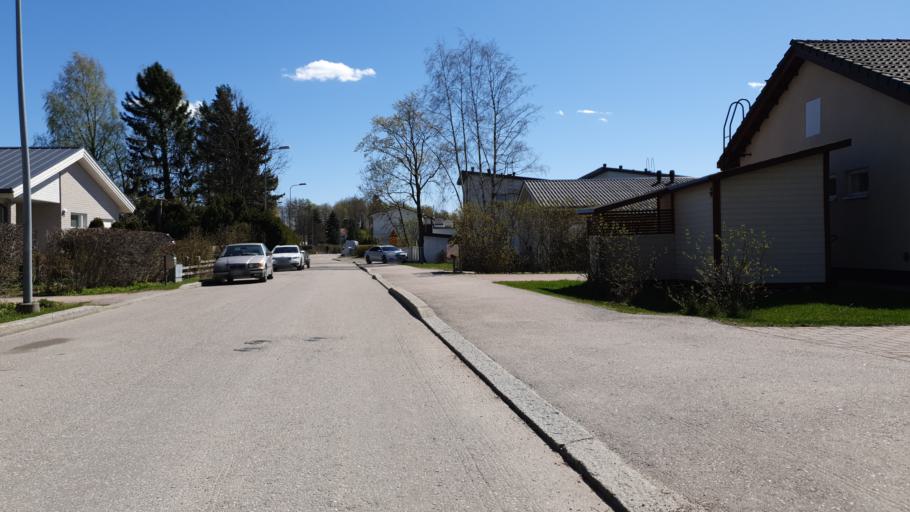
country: FI
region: Uusimaa
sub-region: Helsinki
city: Vantaa
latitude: 60.2622
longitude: 24.9763
